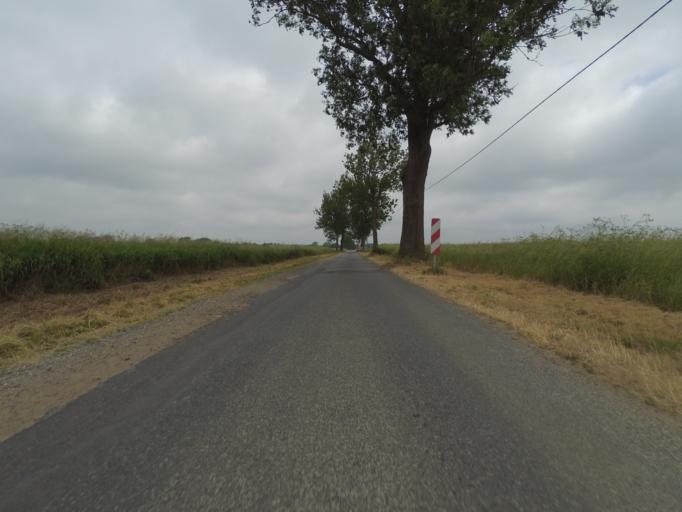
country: DE
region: Mecklenburg-Vorpommern
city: Plau am See
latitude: 53.5244
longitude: 12.2204
